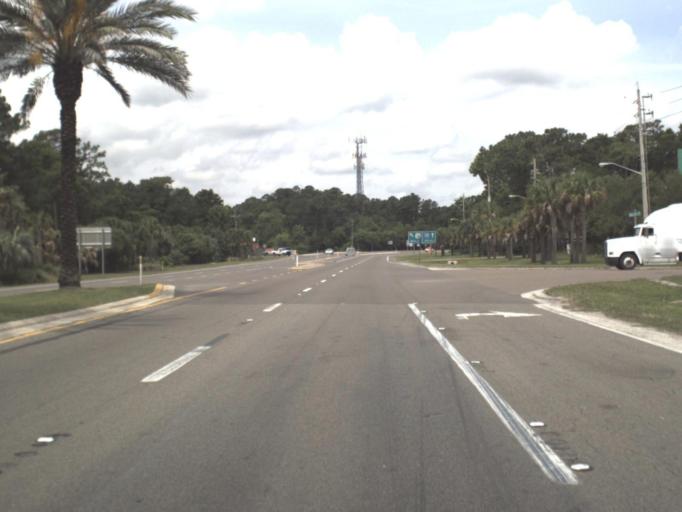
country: US
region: Florida
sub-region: Duval County
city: Jacksonville
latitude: 30.4071
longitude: -81.6426
